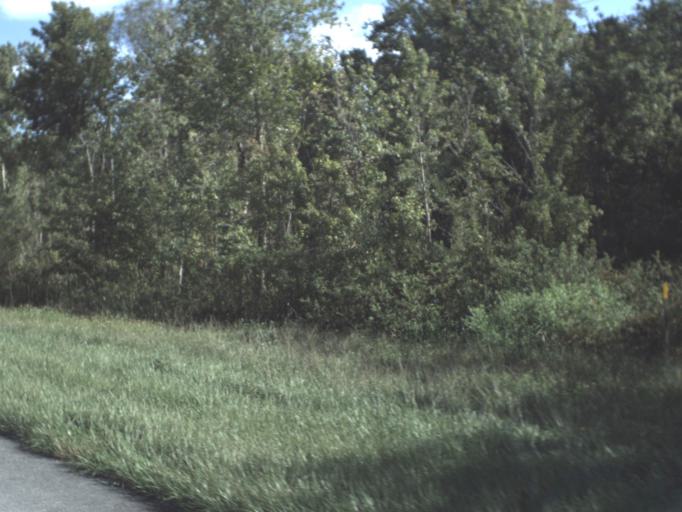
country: US
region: Florida
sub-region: Okeechobee County
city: Cypress Quarters
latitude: 27.5056
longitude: -80.8065
